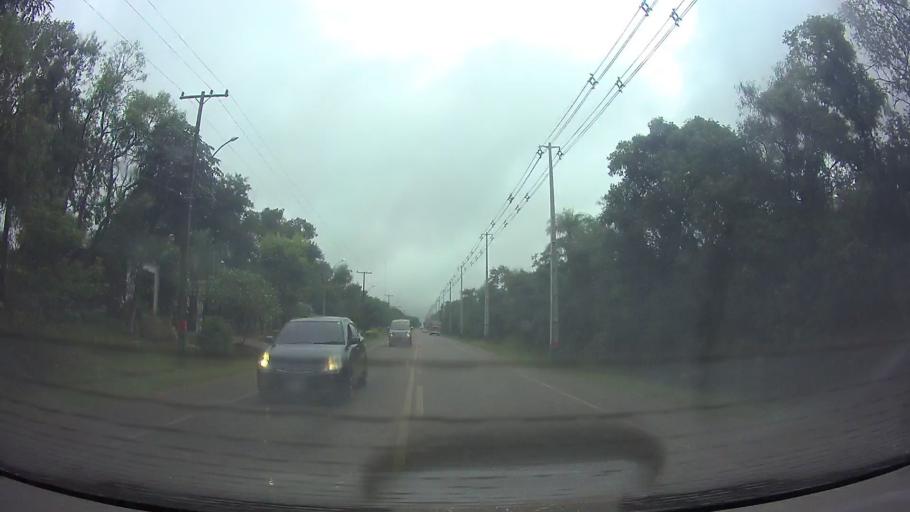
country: PY
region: Cordillera
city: Altos
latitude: -25.2704
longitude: -57.2554
